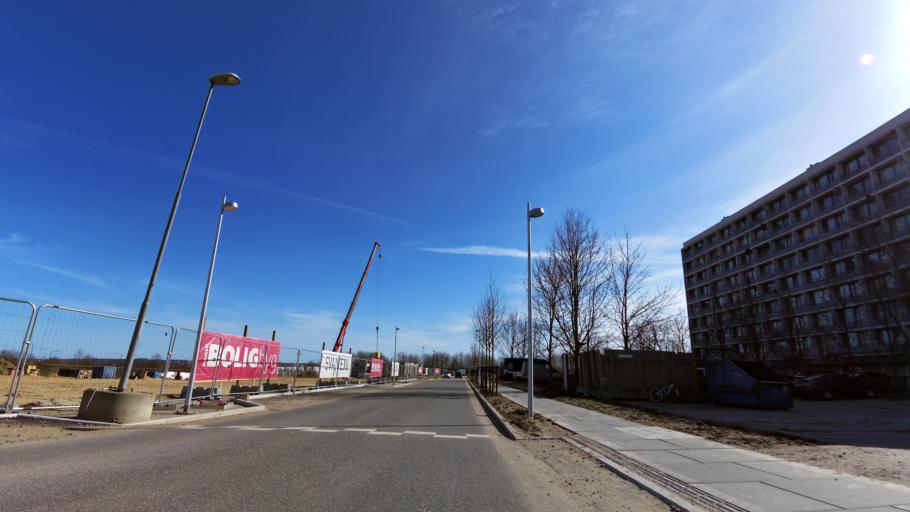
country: DK
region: Central Jutland
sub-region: Arhus Kommune
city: Stavtrup
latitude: 56.1573
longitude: 10.1405
